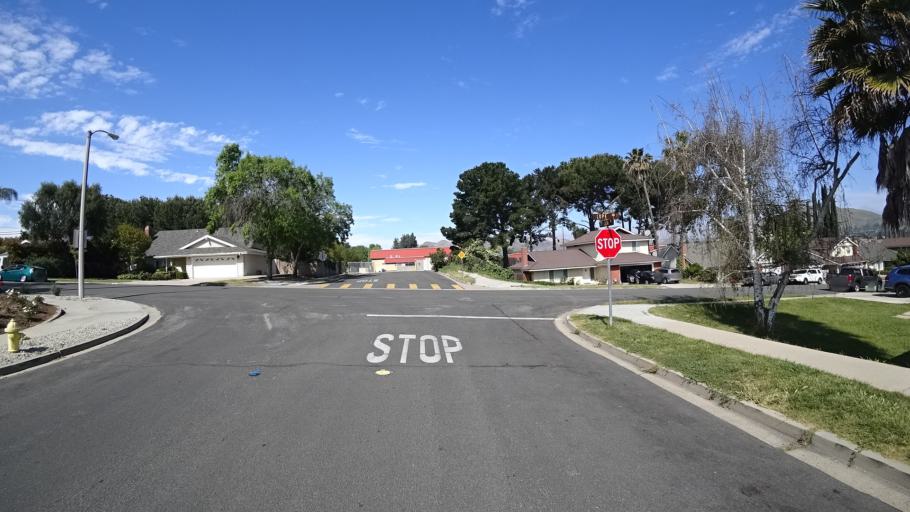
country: US
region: California
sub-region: Ventura County
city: Casa Conejo
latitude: 34.1796
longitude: -118.9352
